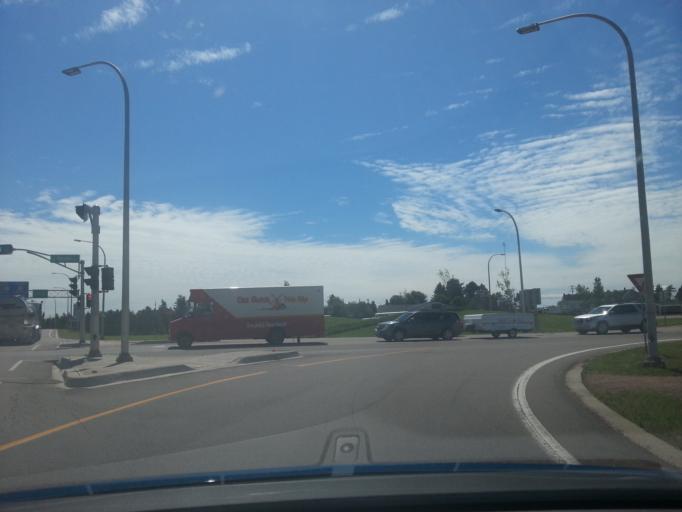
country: CA
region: Prince Edward Island
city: Summerside
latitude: 46.2551
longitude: -63.6886
